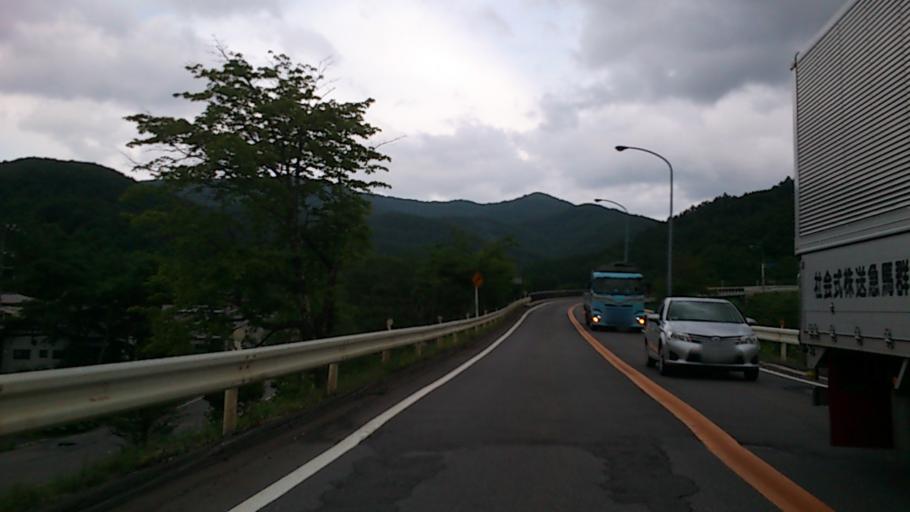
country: JP
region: Nagano
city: Suwa
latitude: 36.1531
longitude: 138.1756
